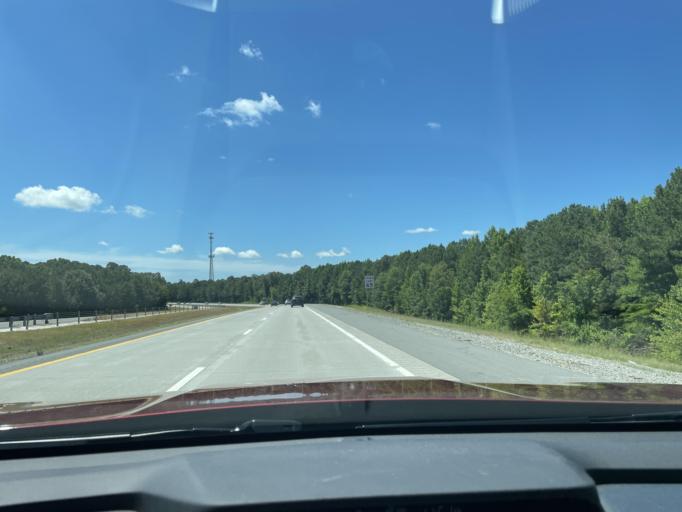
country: US
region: Arkansas
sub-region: Jefferson County
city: Sulphur Springs
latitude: 34.2041
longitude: -92.0723
